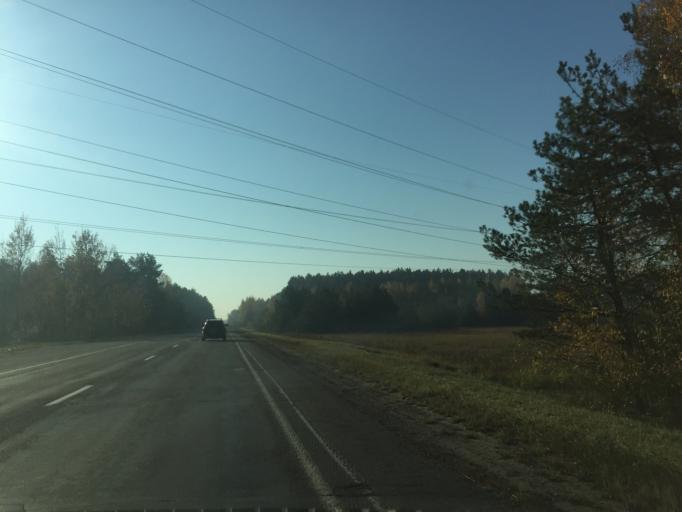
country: BY
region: Gomel
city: Kastsyukowka
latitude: 52.4365
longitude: 30.8263
